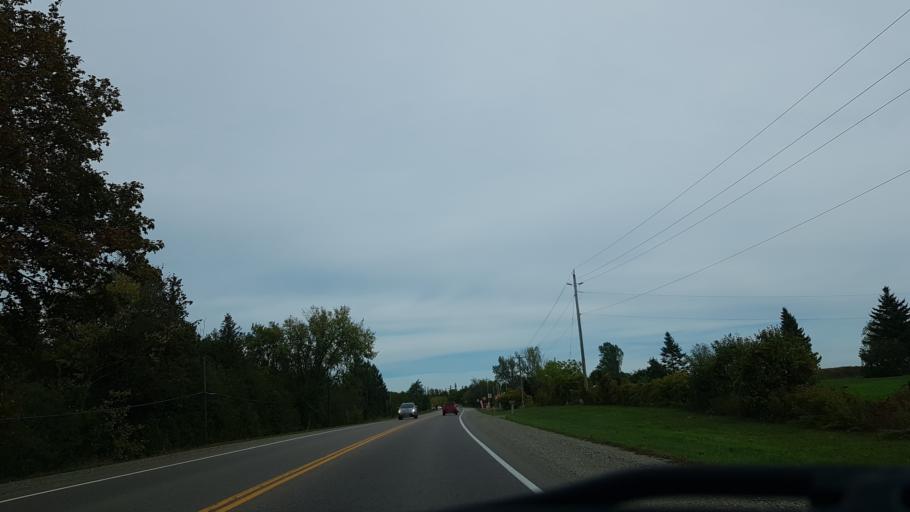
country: CA
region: Ontario
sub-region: Wellington County
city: Guelph
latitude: 43.5938
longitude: -80.2387
